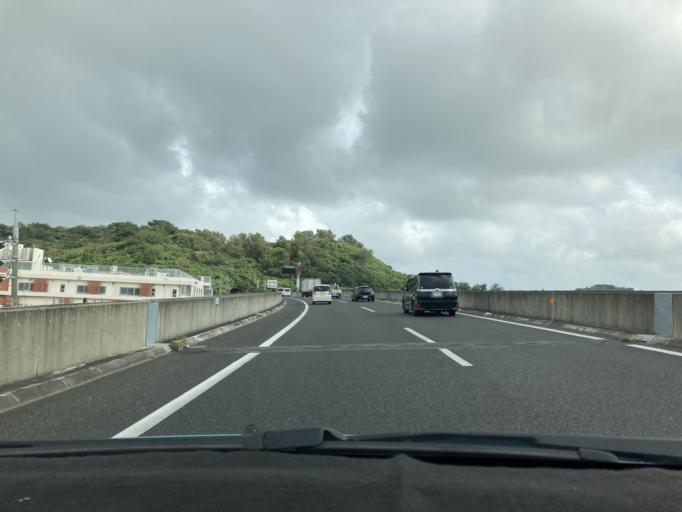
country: JP
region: Okinawa
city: Tomigusuku
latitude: 26.1720
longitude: 127.6774
